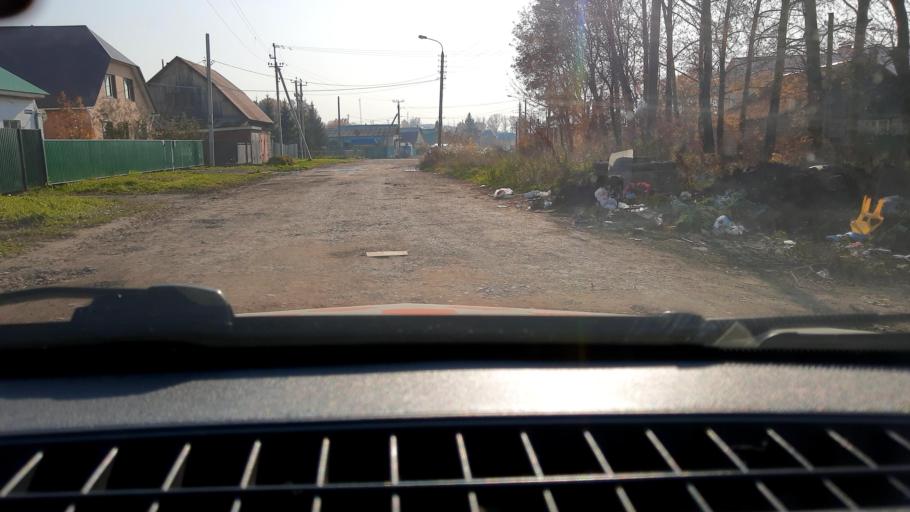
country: RU
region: Bashkortostan
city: Ufa
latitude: 54.8420
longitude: 56.1545
